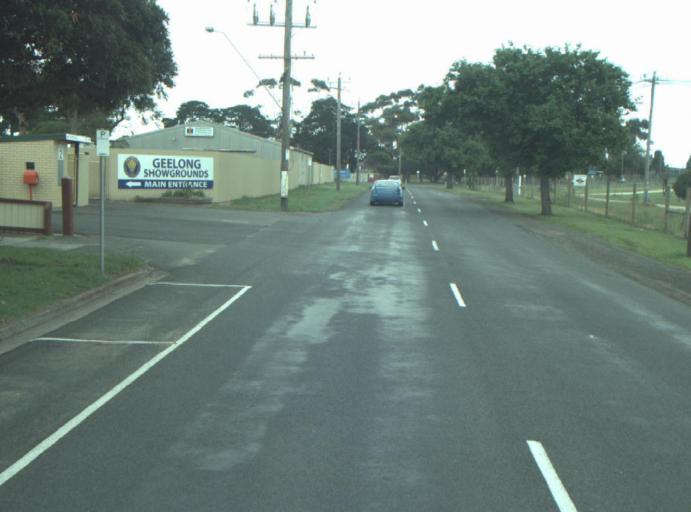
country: AU
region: Victoria
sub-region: Greater Geelong
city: Breakwater
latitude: -38.1708
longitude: 144.3722
